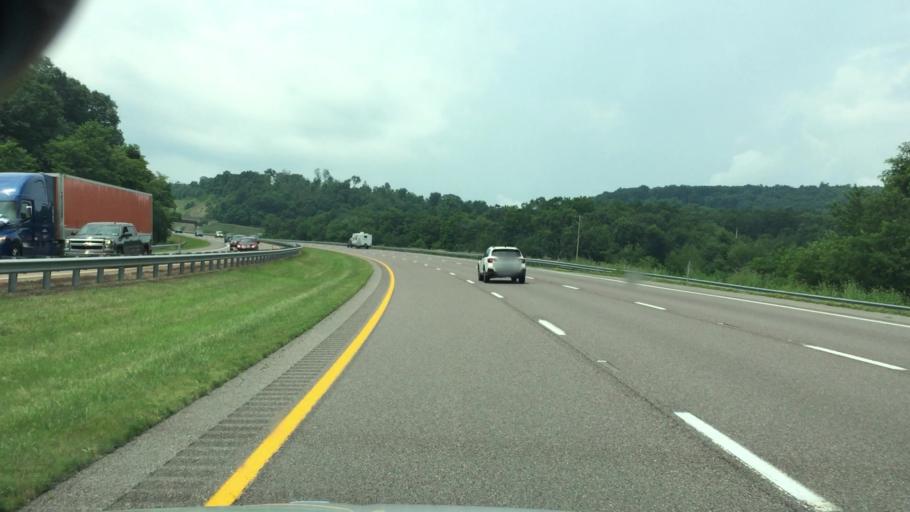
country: US
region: Maryland
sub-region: Allegany County
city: Cumberland
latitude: 39.6918
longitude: -78.5042
